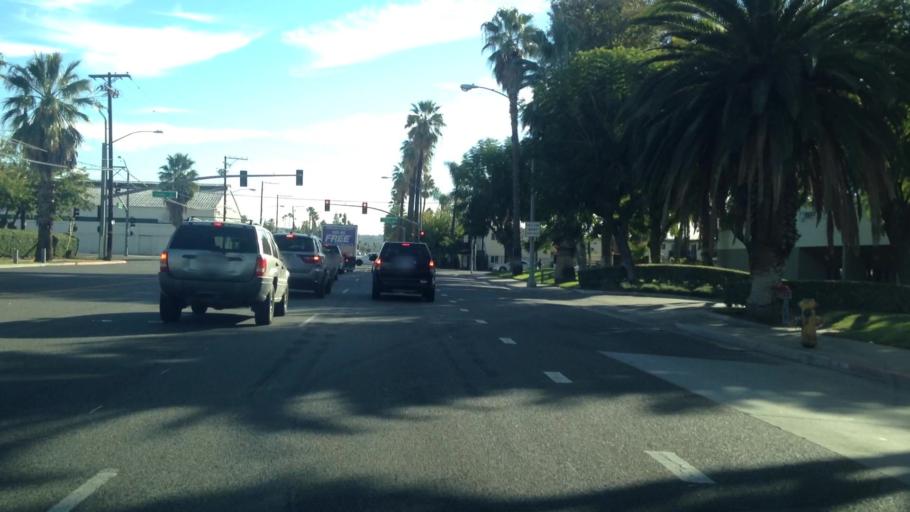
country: US
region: California
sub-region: Riverside County
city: Highgrove
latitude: 33.9803
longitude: -117.3486
